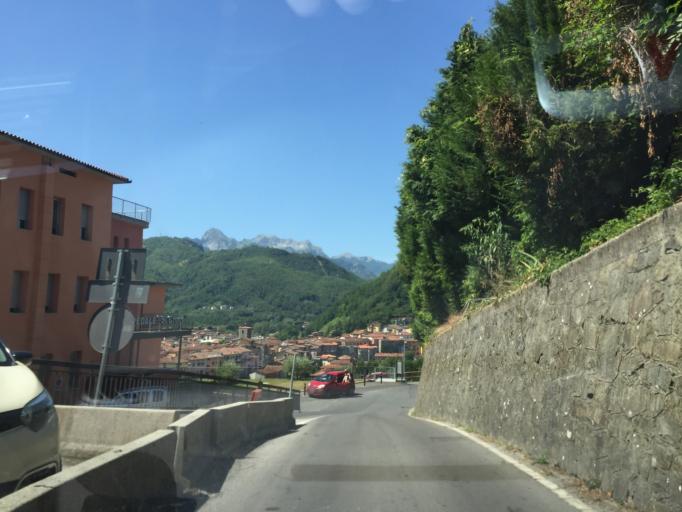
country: IT
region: Tuscany
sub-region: Provincia di Lucca
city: Castelnuovo di Garfagnana
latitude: 44.1127
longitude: 10.4141
